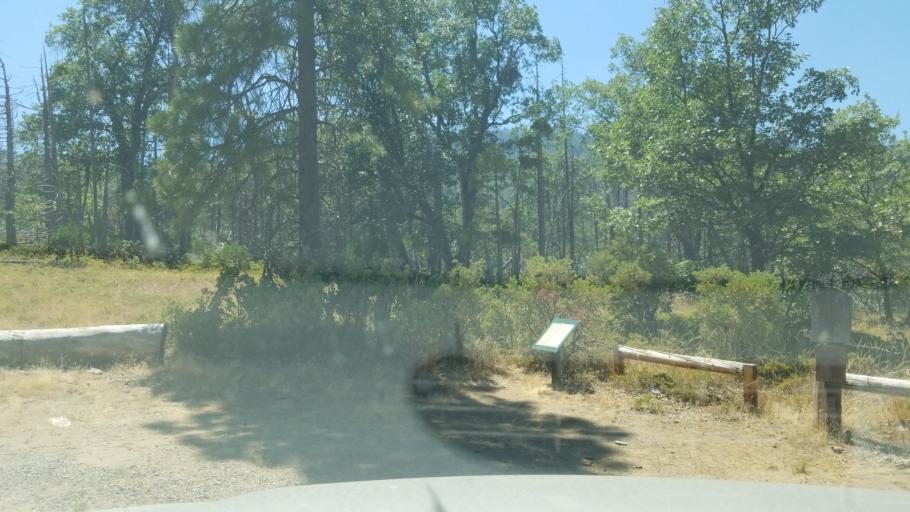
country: US
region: California
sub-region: Fresno County
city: Auberry
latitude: 37.2328
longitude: -119.3647
